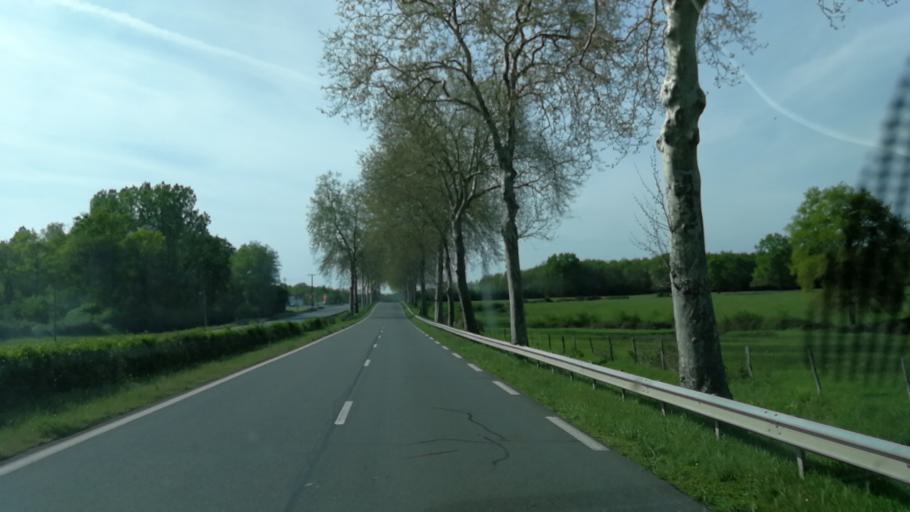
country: FR
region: Bourgogne
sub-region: Departement de la Nievre
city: Chantenay-Saint-Imbert
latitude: 46.7513
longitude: 3.1442
